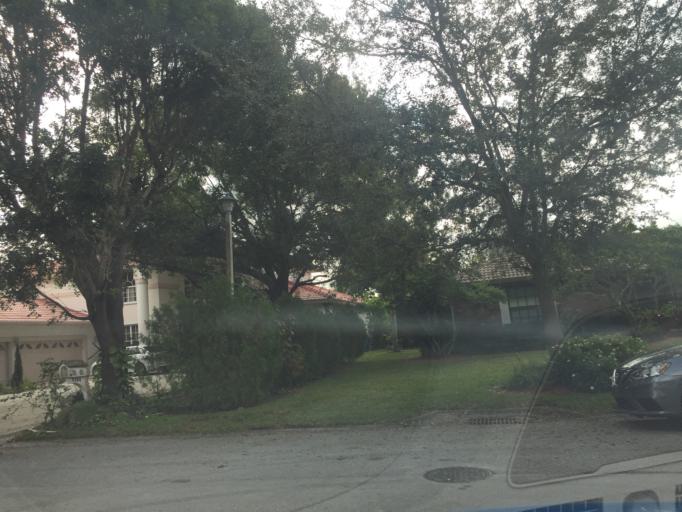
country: US
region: Florida
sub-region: Broward County
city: Tamarac
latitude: 26.2309
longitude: -80.2512
